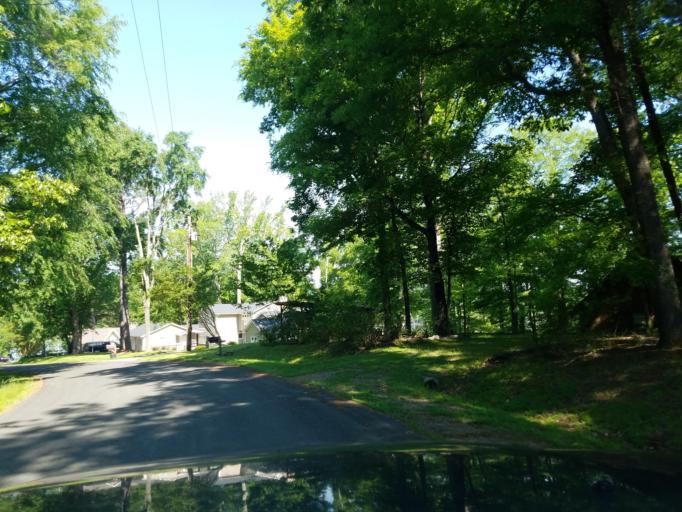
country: US
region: North Carolina
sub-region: Vance County
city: Henderson
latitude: 36.4040
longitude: -78.3910
